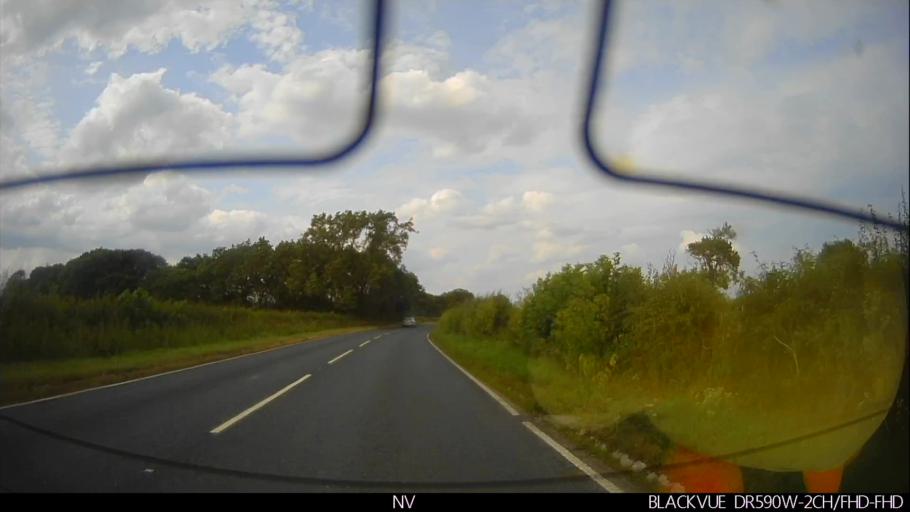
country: GB
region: England
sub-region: North Yorkshire
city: Marishes
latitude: 54.1862
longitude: -0.7638
